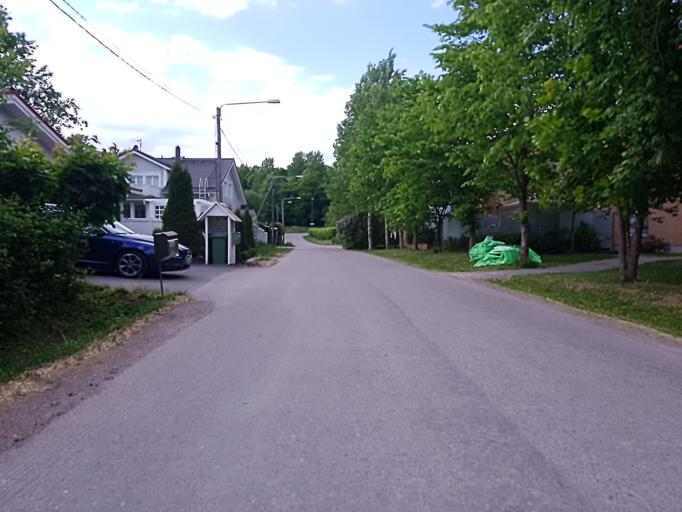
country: FI
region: Uusimaa
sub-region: Helsinki
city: Vantaa
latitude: 60.2748
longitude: 24.9677
